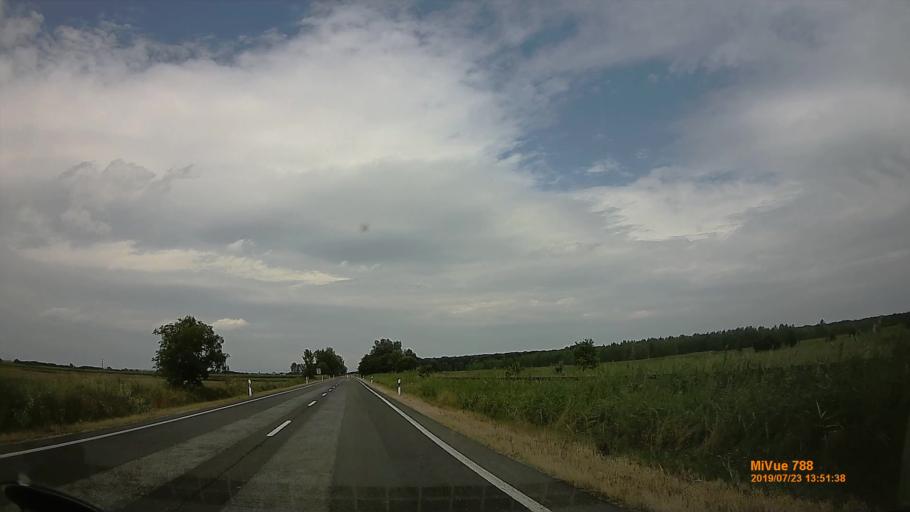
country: HU
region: Hajdu-Bihar
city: Polgar
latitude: 47.8911
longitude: 21.1525
